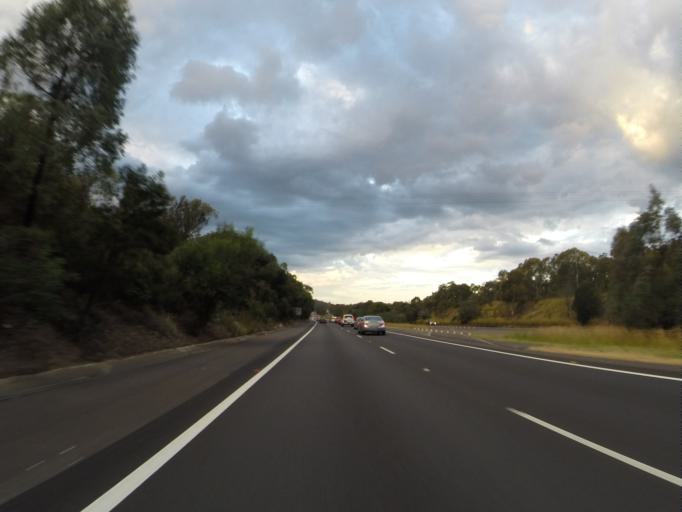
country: AU
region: New South Wales
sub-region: Wollondilly
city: Douglas Park
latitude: -34.1952
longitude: 150.7094
